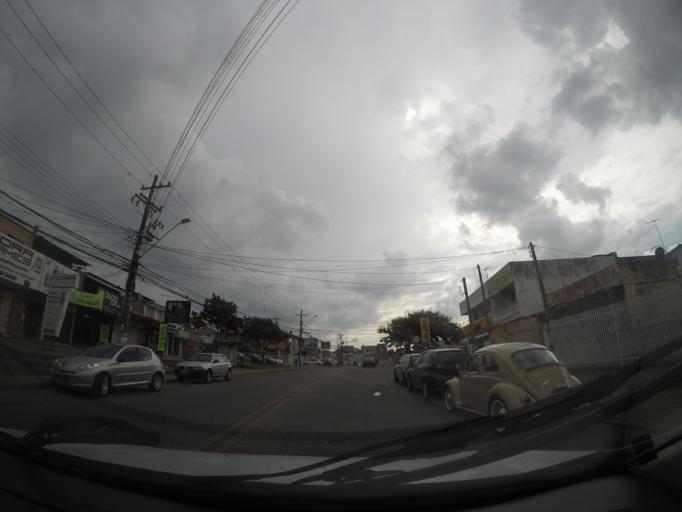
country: BR
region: Parana
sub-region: Sao Jose Dos Pinhais
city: Sao Jose dos Pinhais
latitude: -25.5283
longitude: -49.2495
